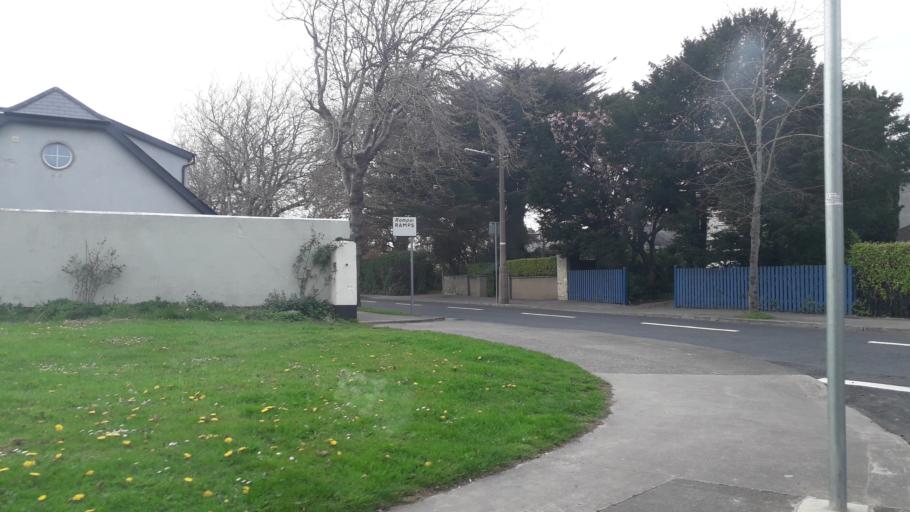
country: IE
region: Leinster
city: Dollymount
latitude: 53.3634
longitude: -6.1884
